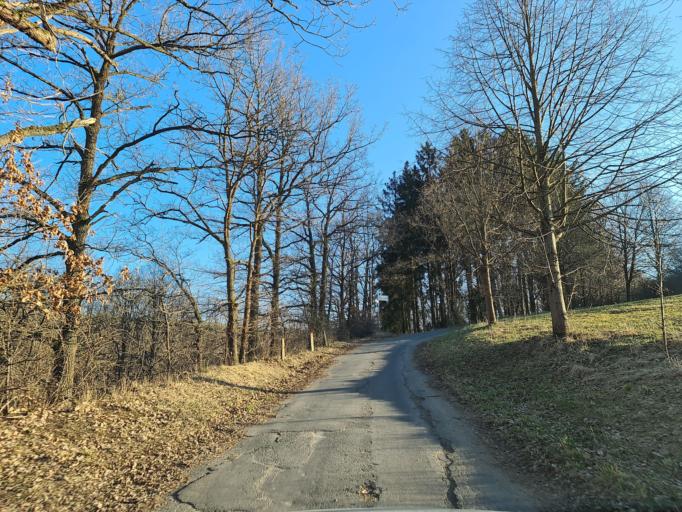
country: DE
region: Saxony
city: Pohl
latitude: 50.5359
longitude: 12.1722
